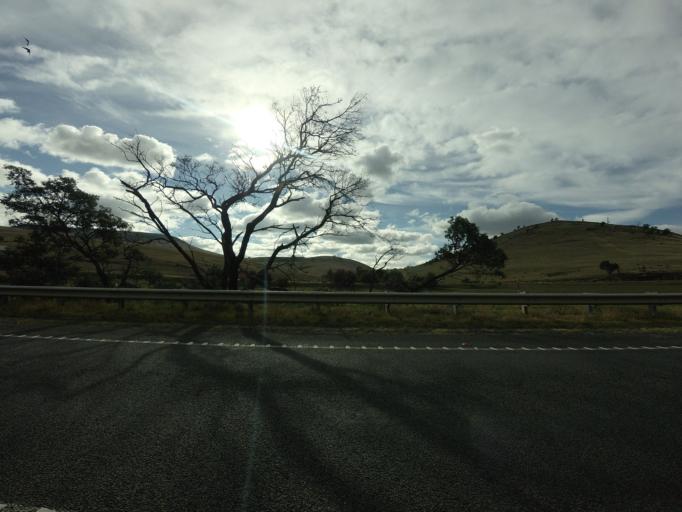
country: AU
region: Tasmania
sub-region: Brighton
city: Bridgewater
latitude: -42.4412
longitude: 147.2319
